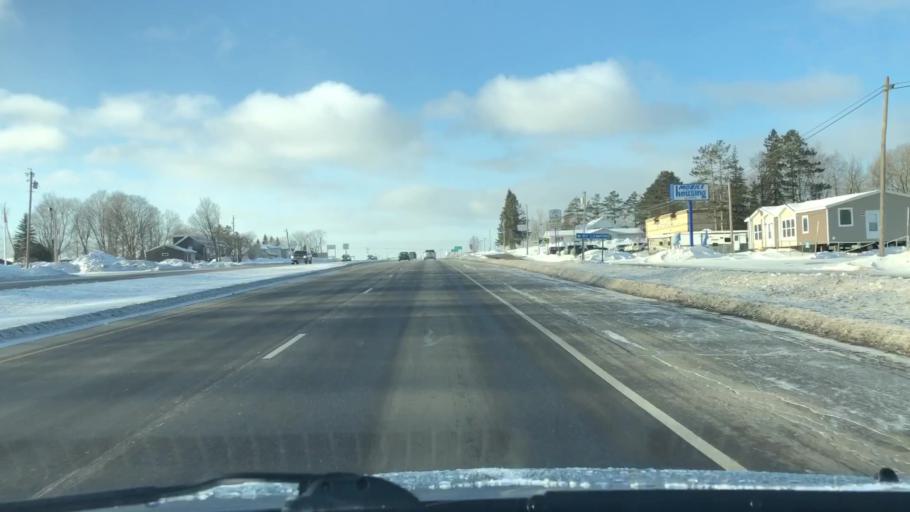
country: US
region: Minnesota
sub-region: Saint Louis County
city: Hermantown
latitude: 46.8241
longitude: -92.1898
